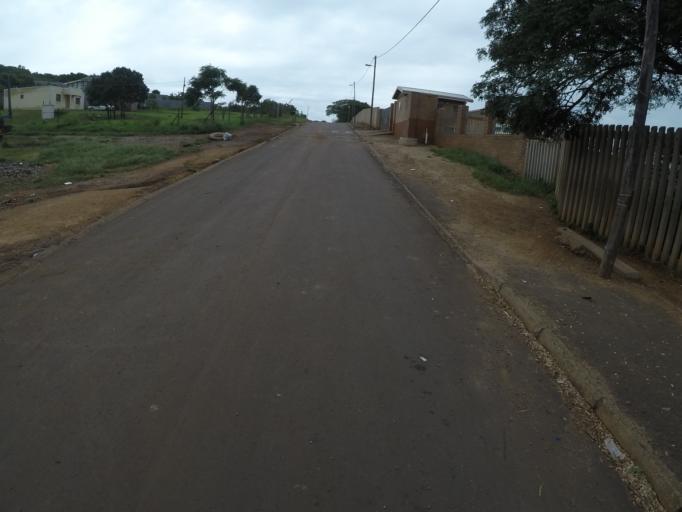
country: ZA
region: KwaZulu-Natal
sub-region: uThungulu District Municipality
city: Empangeni
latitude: -28.7714
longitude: 31.8581
